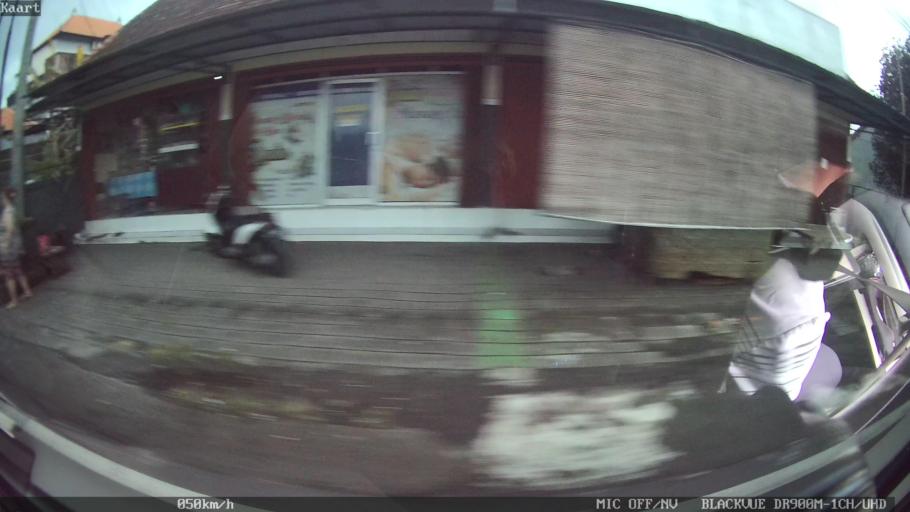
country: ID
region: Bali
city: Banjar Mambalkajanan
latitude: -8.5390
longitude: 115.2235
